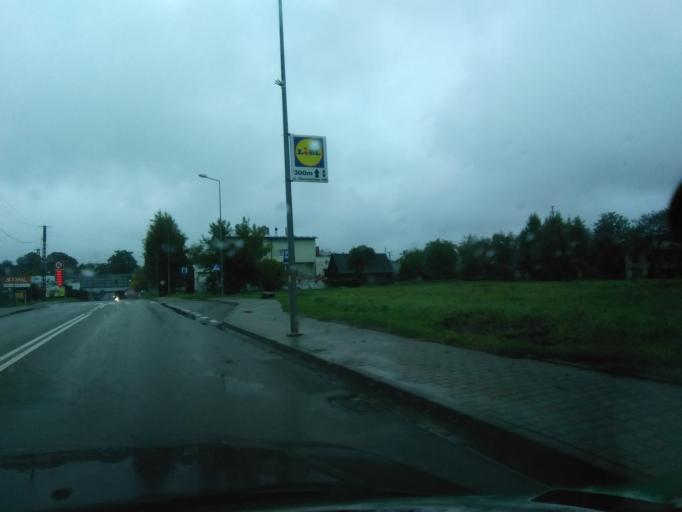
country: PL
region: Subcarpathian Voivodeship
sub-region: Powiat debicki
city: Debica
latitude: 50.0577
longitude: 21.4082
